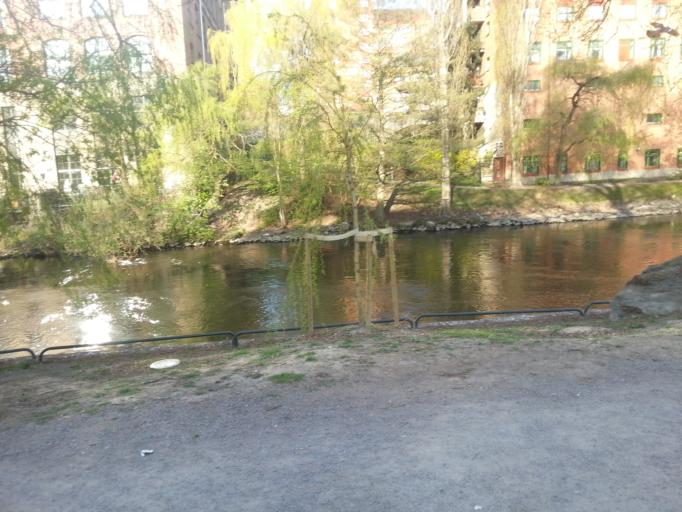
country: SE
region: OEstergoetland
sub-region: Norrkopings Kommun
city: Norrkoping
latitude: 58.5912
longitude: 16.1841
